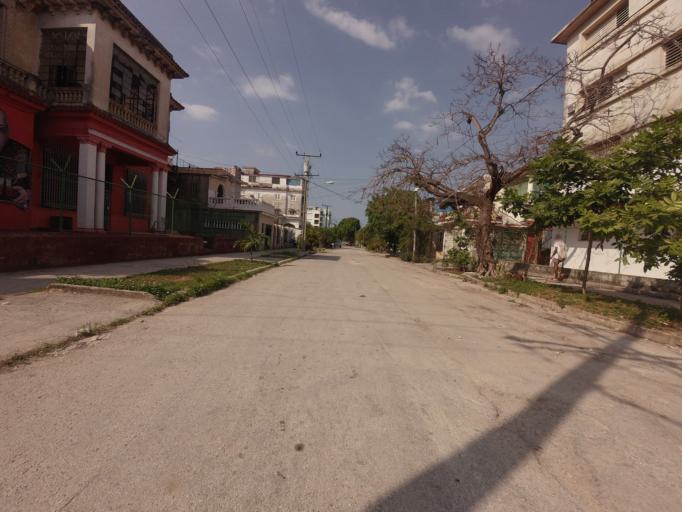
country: CU
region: La Habana
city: Cerro
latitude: 23.1106
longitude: -82.4231
